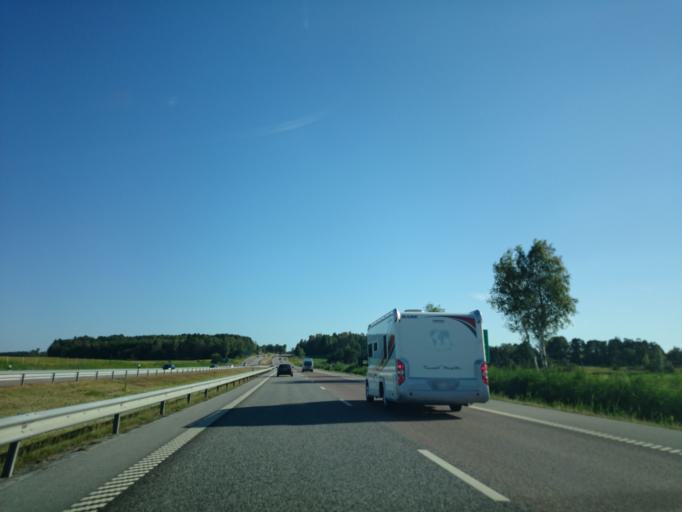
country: SE
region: Stockholm
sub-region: Sodertalje Kommun
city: Pershagen
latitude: 59.0795
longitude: 17.5943
